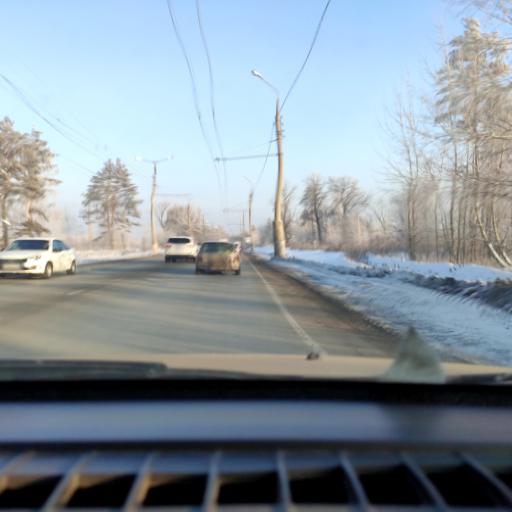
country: RU
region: Samara
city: Tol'yatti
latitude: 53.4852
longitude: 49.3809
